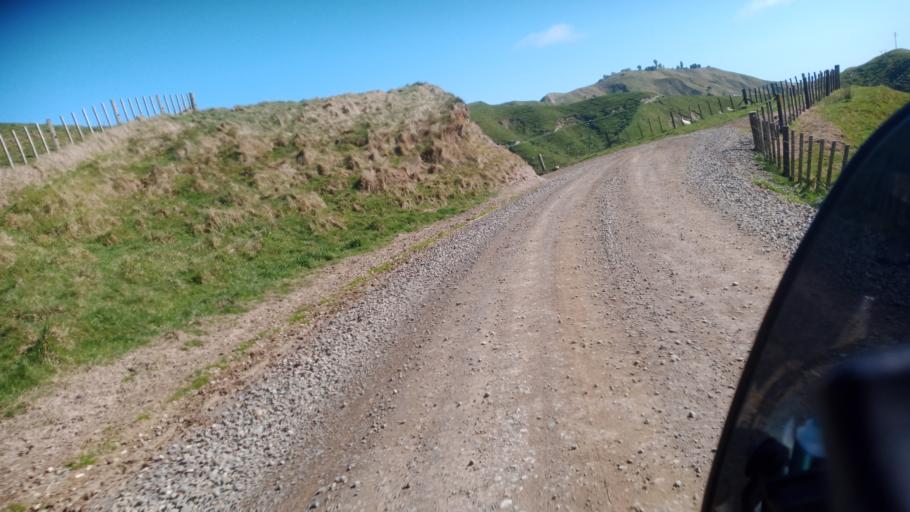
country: NZ
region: Gisborne
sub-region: Gisborne District
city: Gisborne
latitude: -39.1642
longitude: 177.9009
